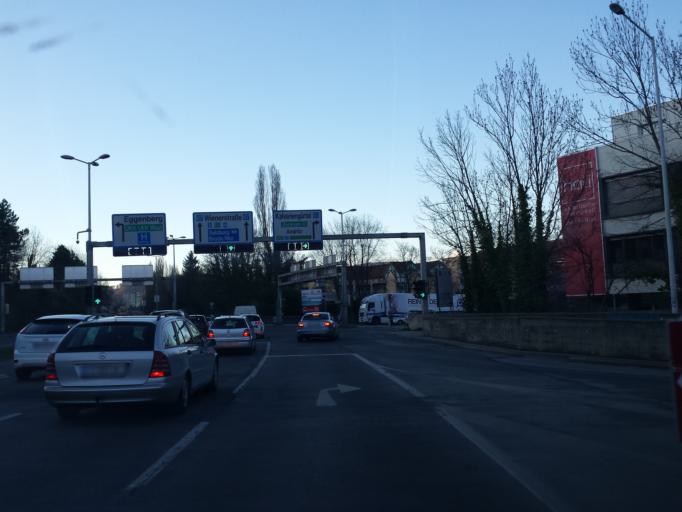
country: AT
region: Styria
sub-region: Graz Stadt
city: Goesting
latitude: 47.0830
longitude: 15.4157
